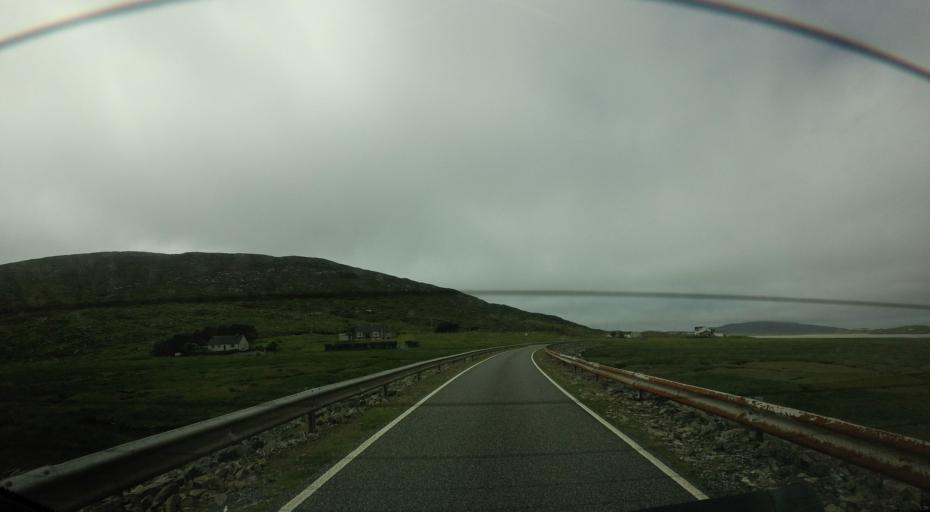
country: GB
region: Scotland
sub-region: Eilean Siar
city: Harris
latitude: 57.8652
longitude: -6.9218
